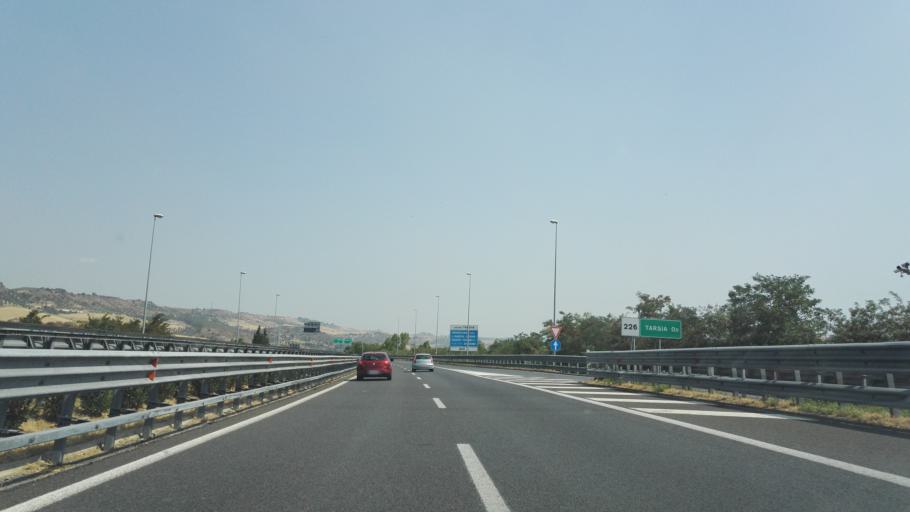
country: IT
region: Calabria
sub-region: Provincia di Cosenza
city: Tarsia
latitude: 39.5803
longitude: 16.2442
